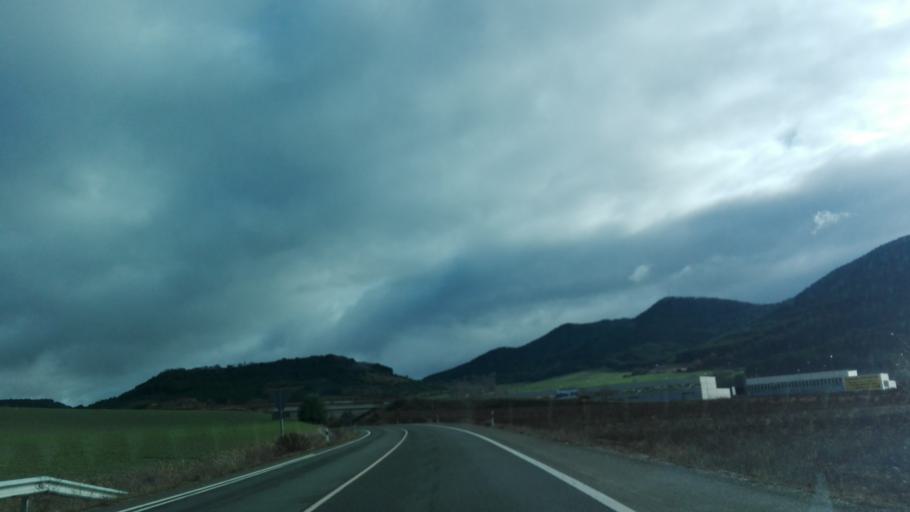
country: ES
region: Navarre
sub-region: Provincia de Navarra
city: Egues-Uharte
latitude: 42.8240
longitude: -1.5570
